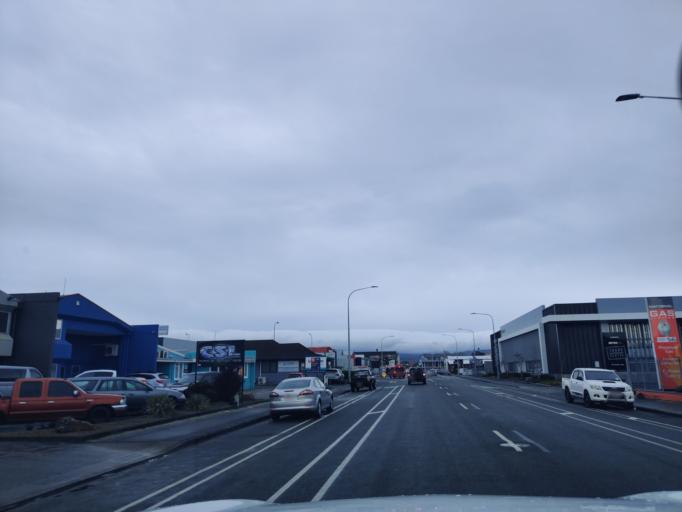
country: NZ
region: Manawatu-Wanganui
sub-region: Palmerston North City
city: Palmerston North
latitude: -40.3544
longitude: 175.6034
